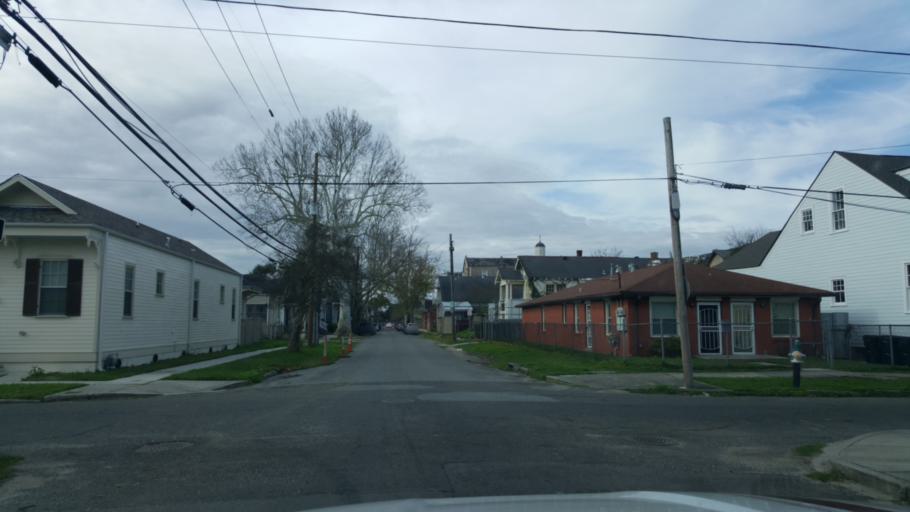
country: US
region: Louisiana
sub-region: Orleans Parish
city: New Orleans
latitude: 29.9753
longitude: -90.0691
